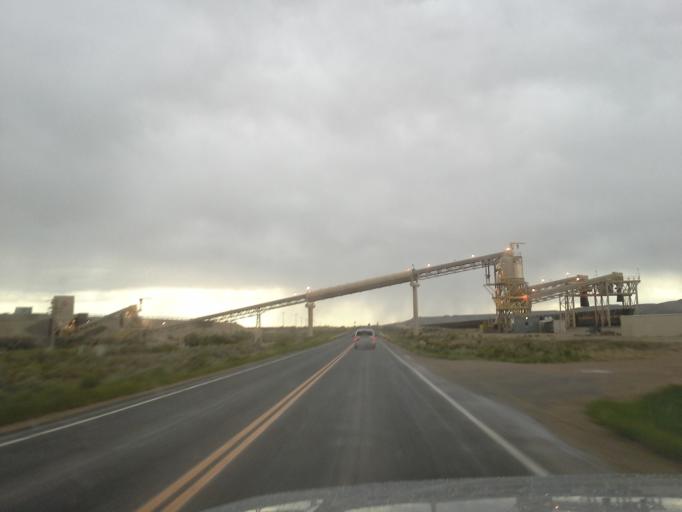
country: US
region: Wyoming
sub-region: Park County
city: Powell
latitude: 45.0576
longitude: -108.6573
